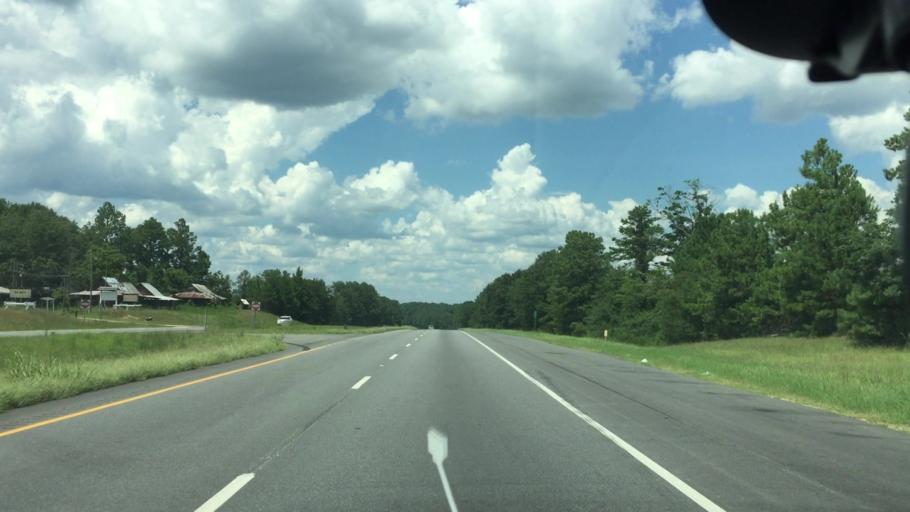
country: US
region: Alabama
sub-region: Pike County
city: Troy
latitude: 31.9005
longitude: -86.0106
